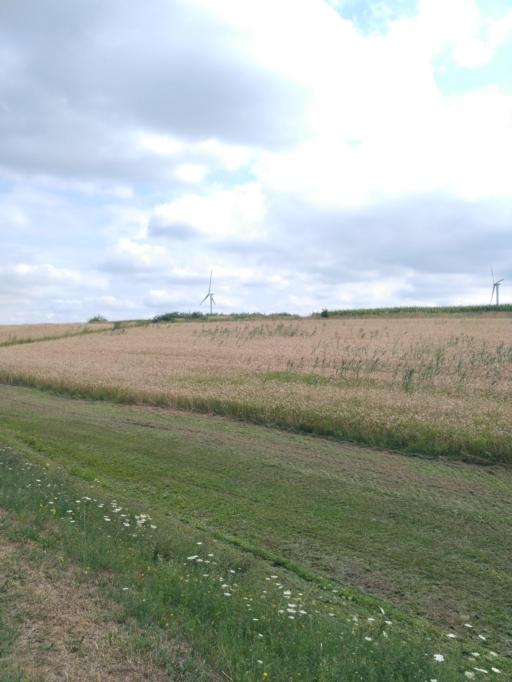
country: PL
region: Subcarpathian Voivodeship
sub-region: Powiat krosnienski
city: Rymanow
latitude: 49.5967
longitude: 21.8466
